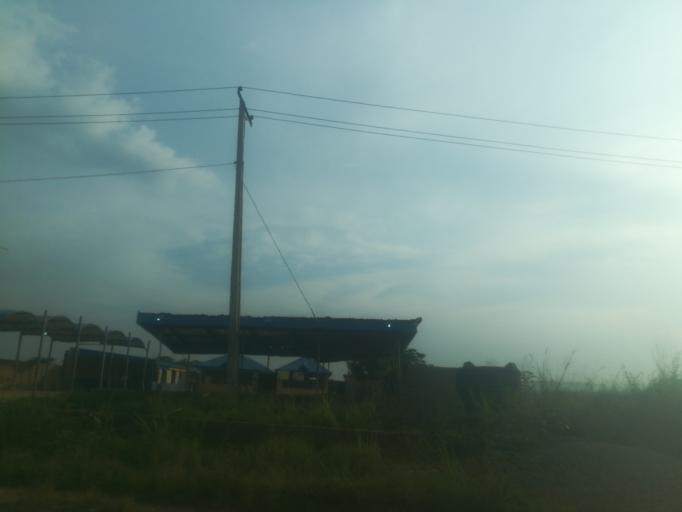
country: NG
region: Ogun
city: Abeokuta
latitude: 7.1679
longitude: 3.2996
